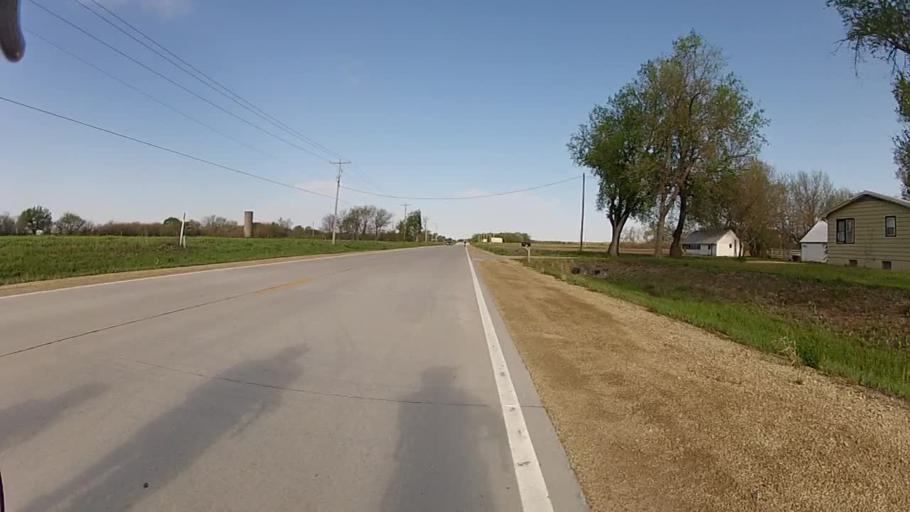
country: US
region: Kansas
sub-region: Riley County
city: Ogden
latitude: 39.1532
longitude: -96.6697
